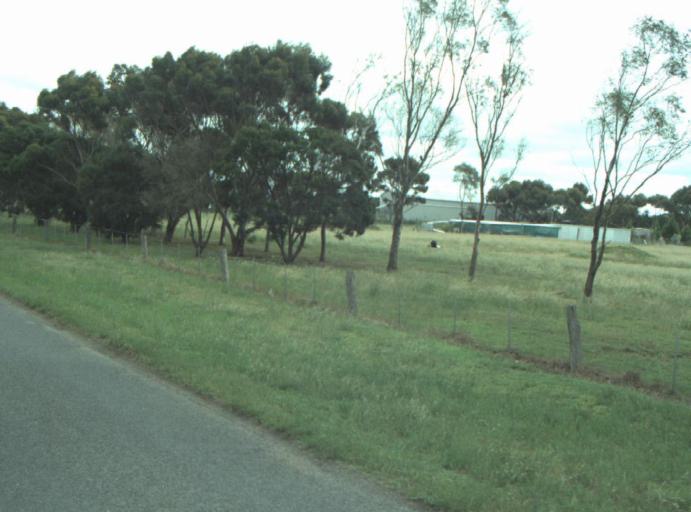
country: AU
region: Victoria
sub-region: Greater Geelong
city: Bell Post Hill
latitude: -38.0580
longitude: 144.3203
